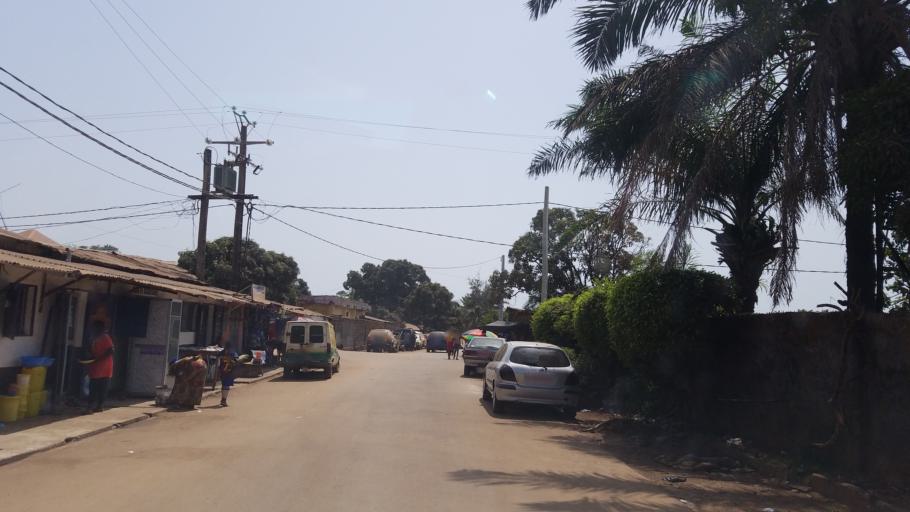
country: GN
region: Conakry
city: Conakry
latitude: 9.5767
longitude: -13.6581
